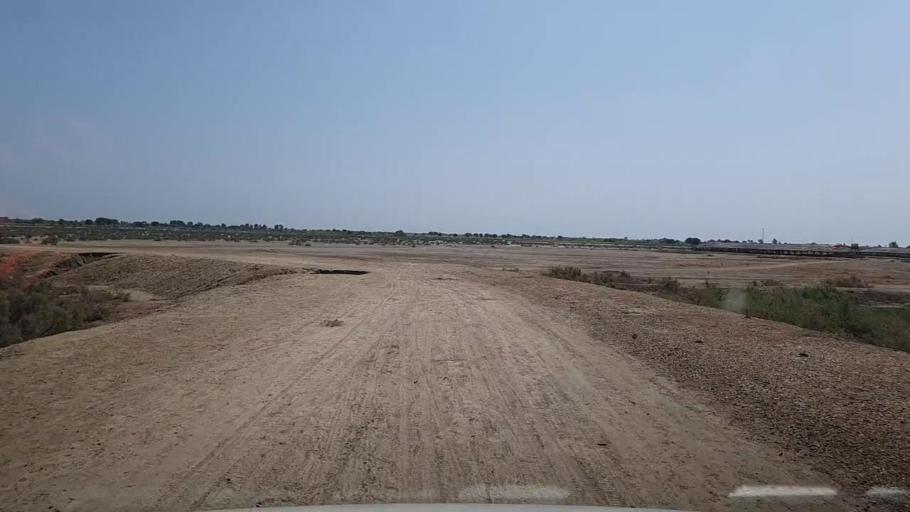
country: PK
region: Sindh
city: Kario
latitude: 24.8275
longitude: 68.7128
